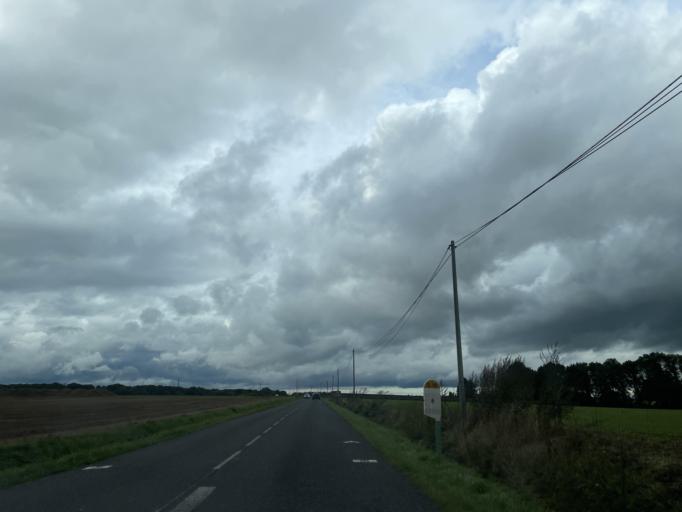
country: FR
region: Ile-de-France
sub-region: Departement de Seine-et-Marne
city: Saint-Jean-les-Deux-Jumeaux
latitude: 48.9021
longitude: 3.0335
